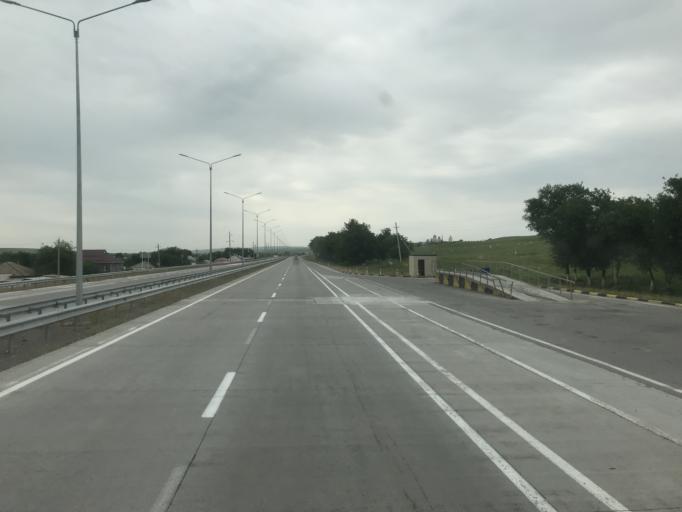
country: KZ
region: Ongtustik Qazaqstan
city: Qazyqurt
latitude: 41.8846
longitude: 69.4408
